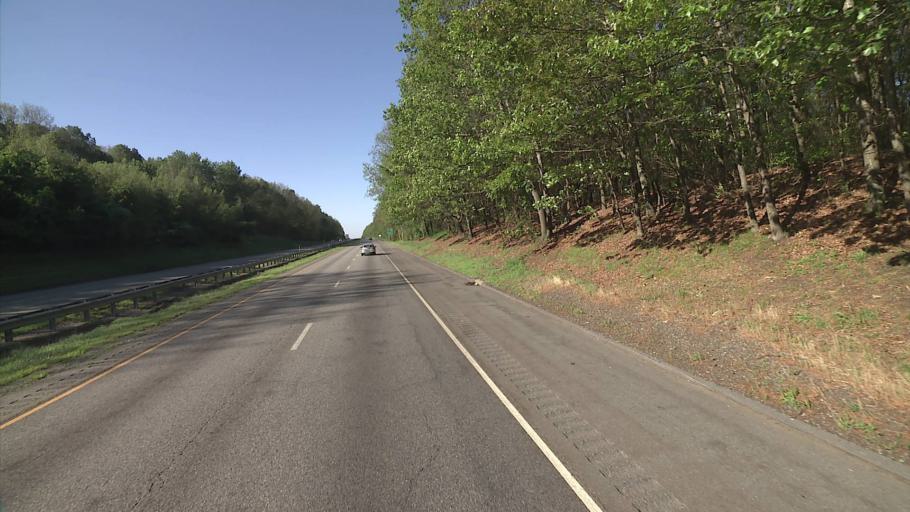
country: US
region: Connecticut
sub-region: Windham County
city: Moosup
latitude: 41.7006
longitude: -71.9020
